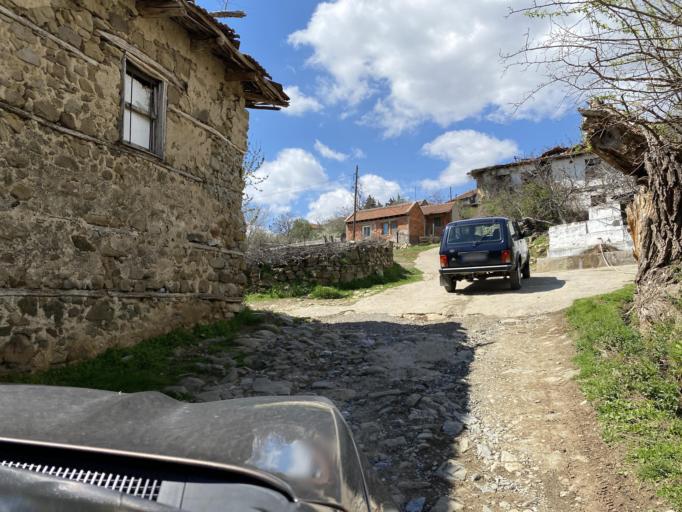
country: MK
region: Caska
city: Caska
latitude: 41.7350
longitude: 21.6417
